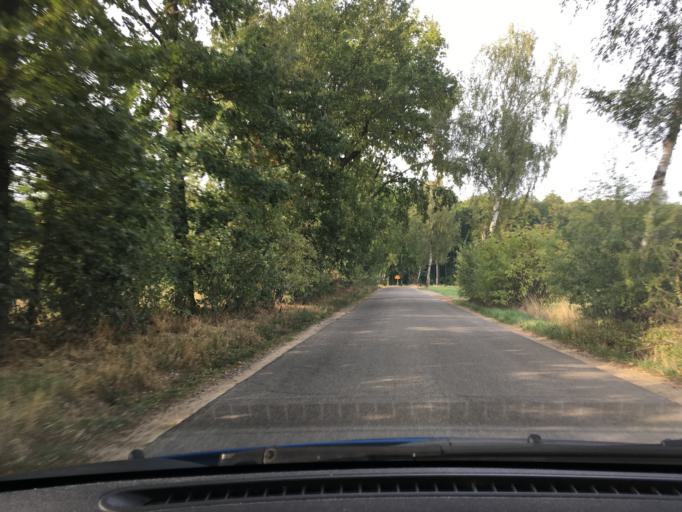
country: DE
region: Lower Saxony
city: Toppenstedt
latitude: 53.3113
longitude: 10.0946
